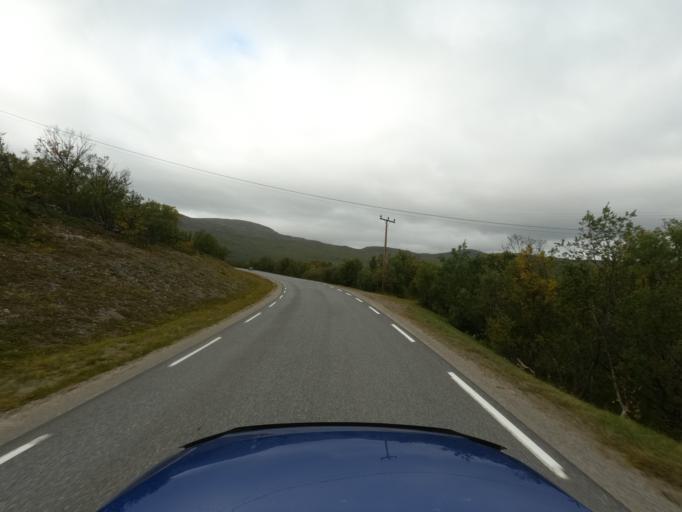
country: NO
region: Finnmark Fylke
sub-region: Porsanger
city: Lakselv
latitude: 70.3479
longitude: 25.0674
